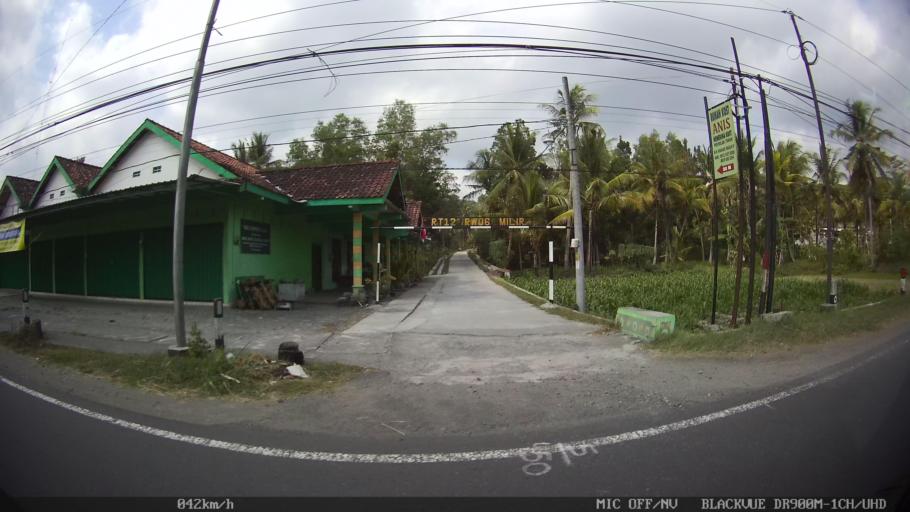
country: ID
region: Daerah Istimewa Yogyakarta
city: Srandakan
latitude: -7.8696
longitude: 110.1866
